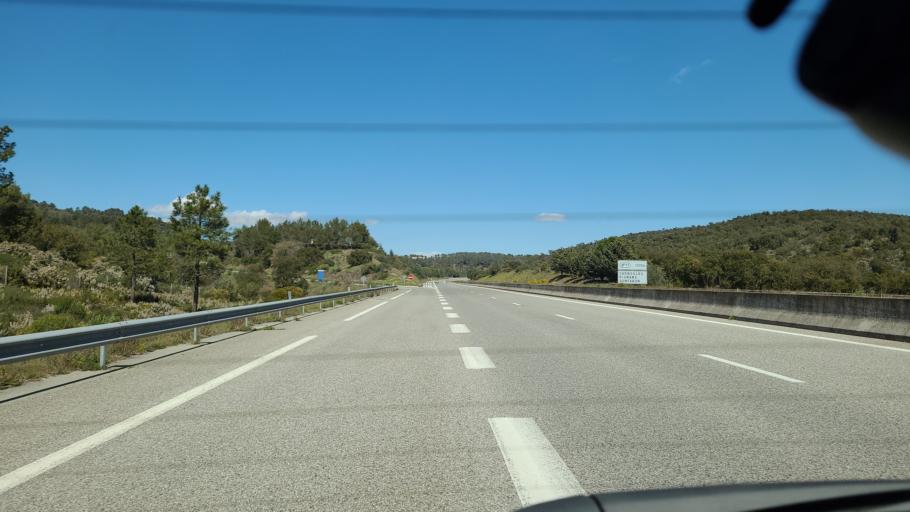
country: FR
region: Provence-Alpes-Cote d'Azur
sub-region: Departement du Var
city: Carnoules
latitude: 43.2795
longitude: 6.1875
